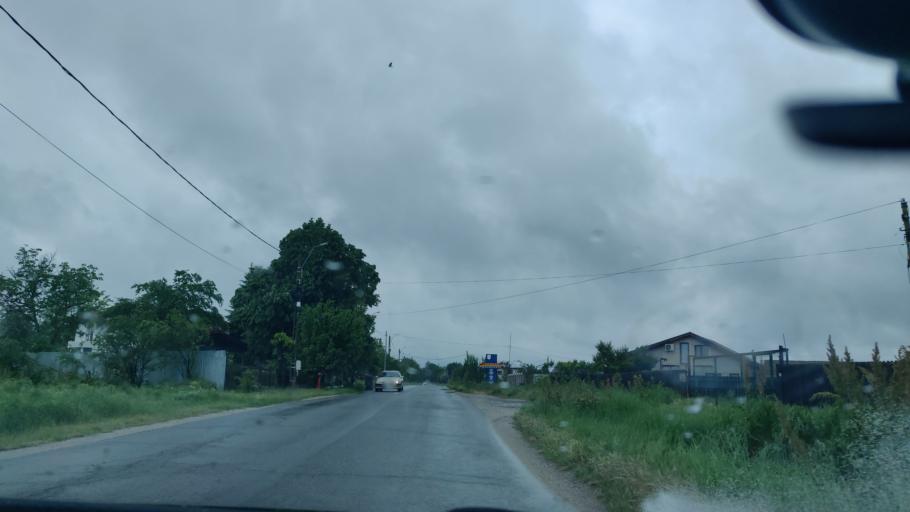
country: RO
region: Giurgiu
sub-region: Comuna Bulbucata
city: Bulbucata
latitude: 44.2732
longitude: 25.8313
